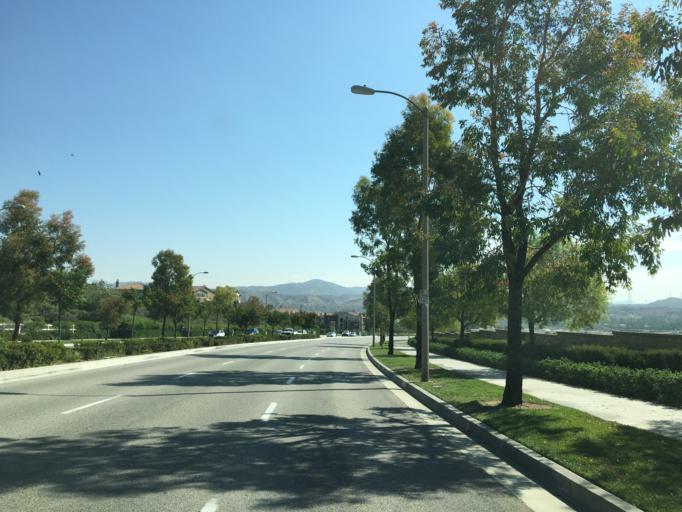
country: US
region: California
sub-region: Los Angeles County
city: Valencia
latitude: 34.4595
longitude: -118.5649
